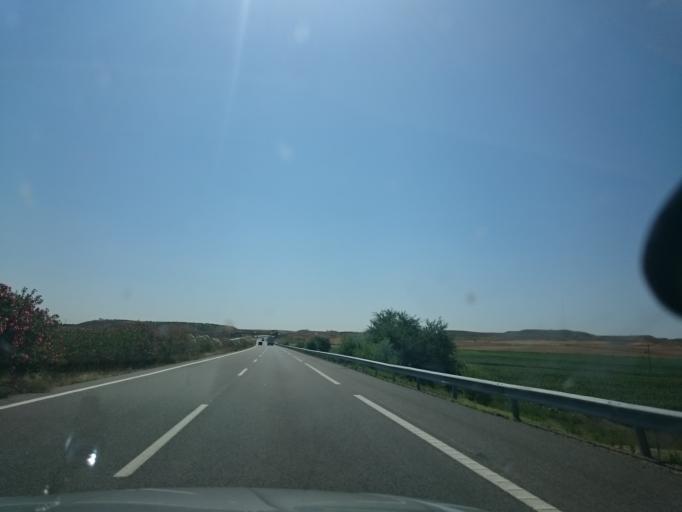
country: ES
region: Navarre
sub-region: Provincia de Navarra
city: Fontellas
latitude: 41.9833
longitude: -1.5643
